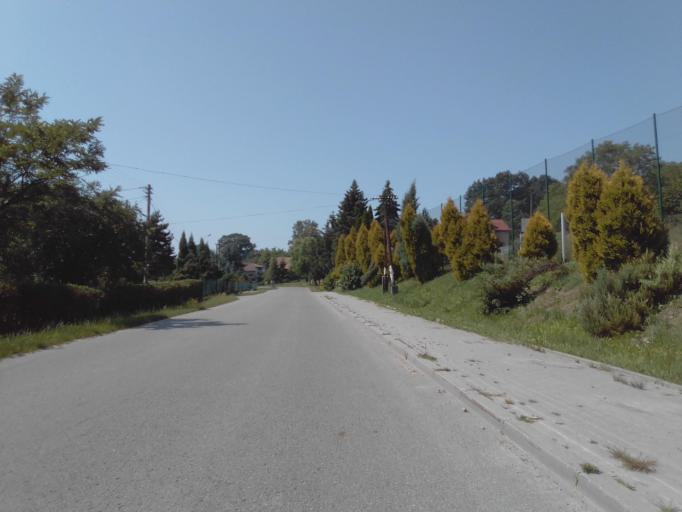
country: PL
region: Subcarpathian Voivodeship
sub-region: Powiat ropczycko-sedziszowski
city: Zagorzyce
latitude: 50.0443
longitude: 21.6569
